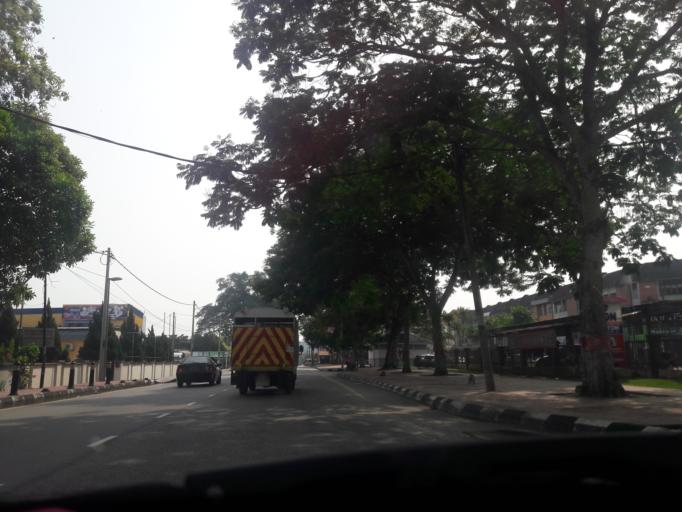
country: MY
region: Kedah
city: Kulim
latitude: 5.3681
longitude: 100.5532
